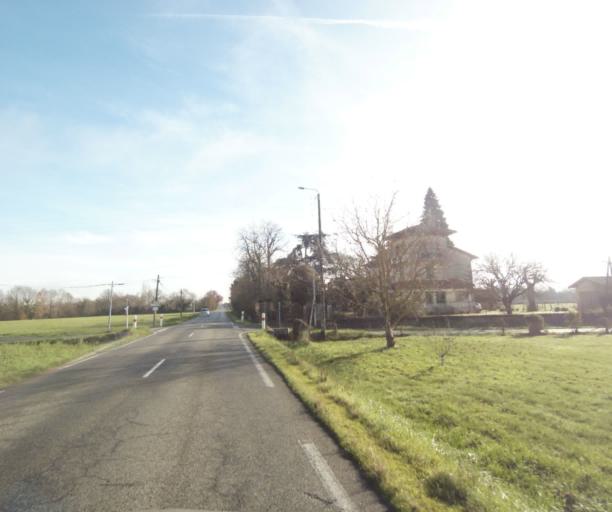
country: FR
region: Midi-Pyrenees
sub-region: Departement du Tarn-et-Garonne
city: Nohic
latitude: 43.8704
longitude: 1.4663
